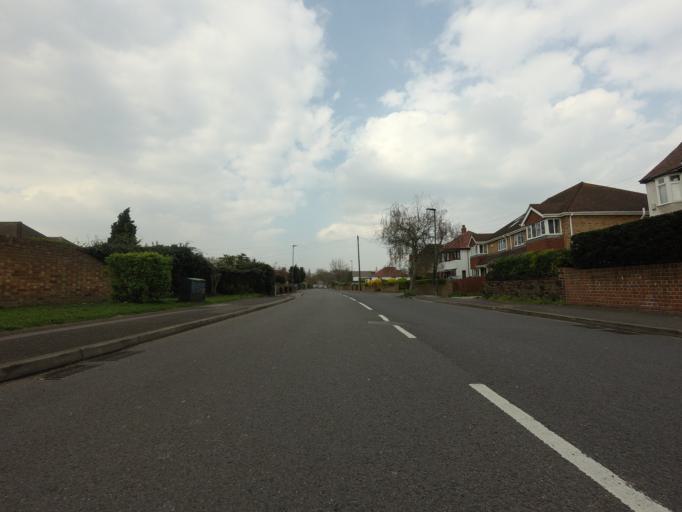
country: GB
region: England
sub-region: Greater London
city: Orpington
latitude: 51.3977
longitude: 0.1158
